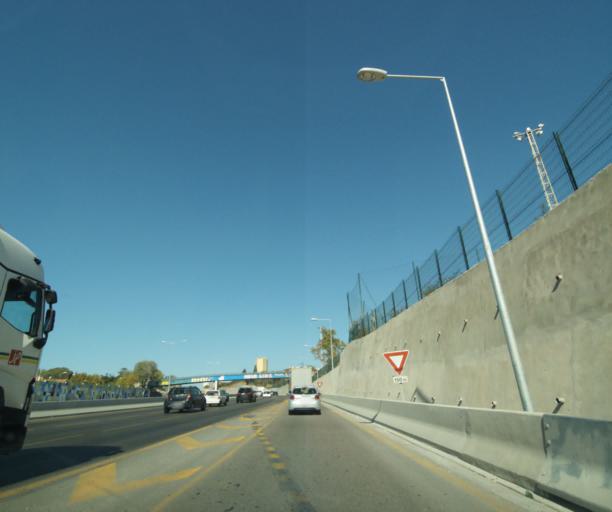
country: FR
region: Provence-Alpes-Cote d'Azur
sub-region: Departement des Bouches-du-Rhone
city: Marseille 14
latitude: 43.3422
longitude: 5.3765
